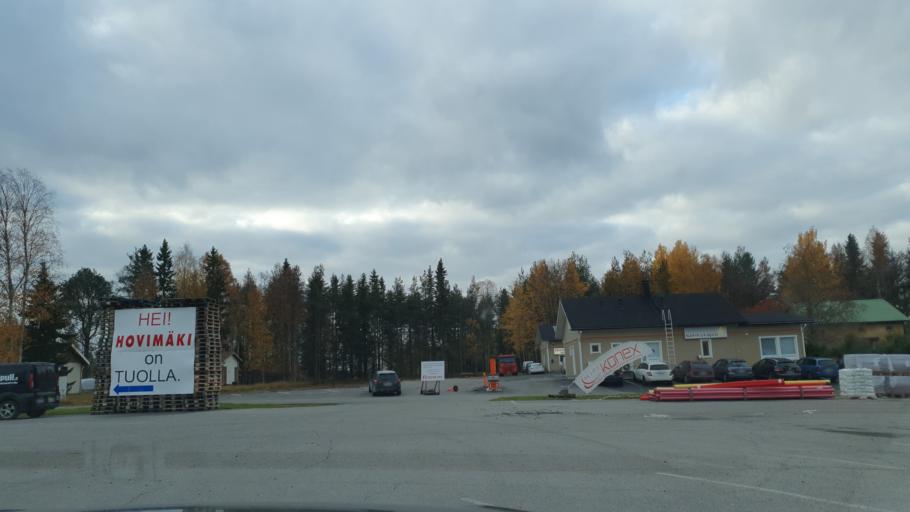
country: FI
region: Lapland
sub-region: Rovaniemi
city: Rovaniemi
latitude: 66.4909
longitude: 25.6829
